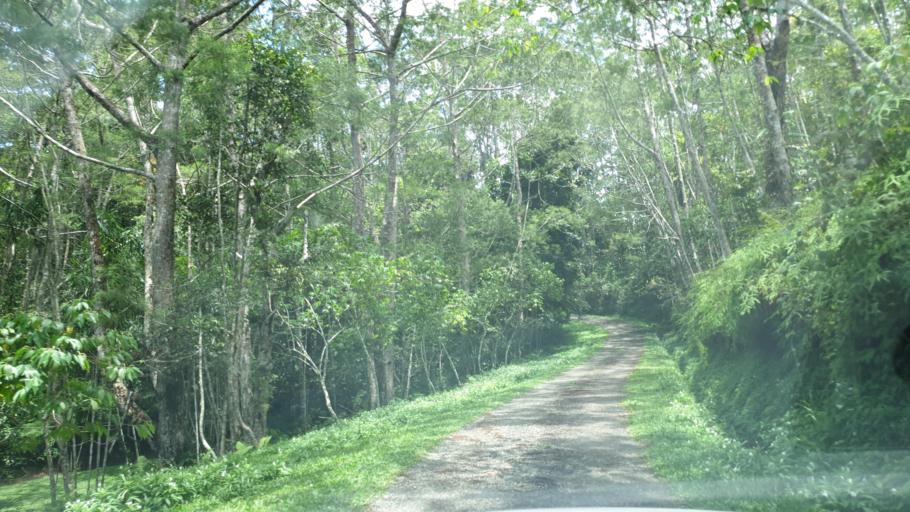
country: PG
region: National Capital
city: Port Moresby
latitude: -9.4355
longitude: 147.3643
